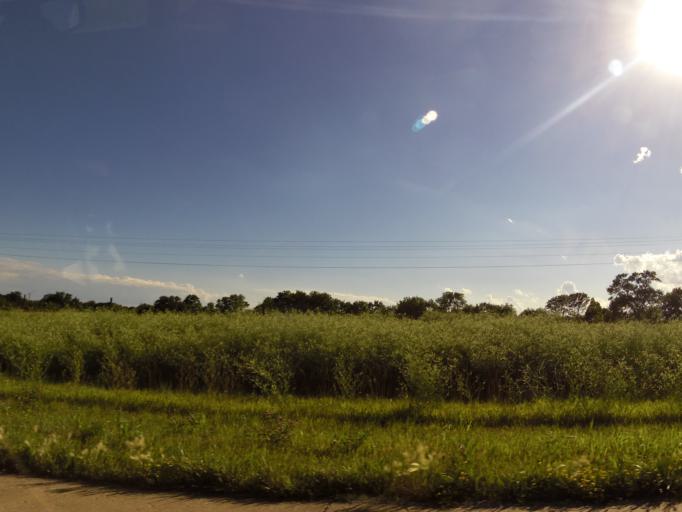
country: US
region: Missouri
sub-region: Ralls County
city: New London
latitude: 39.5657
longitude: -91.3922
